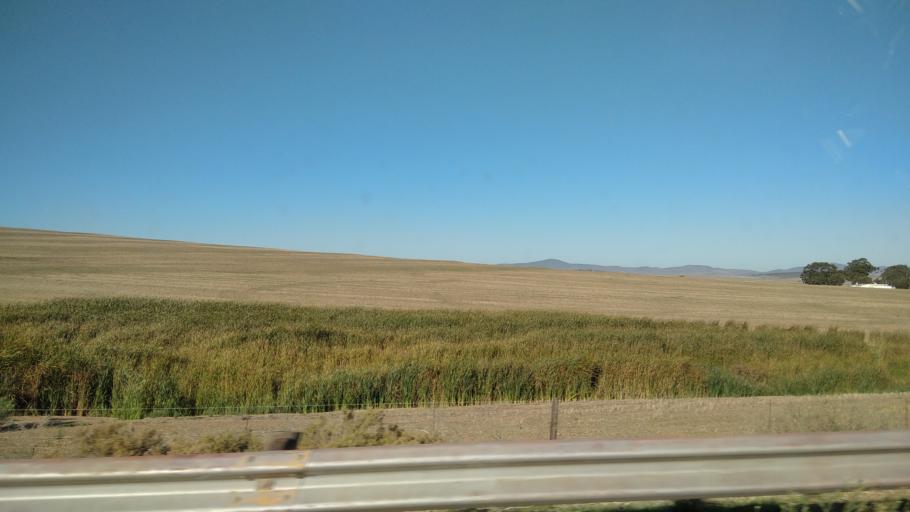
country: ZA
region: Western Cape
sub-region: West Coast District Municipality
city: Malmesbury
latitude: -33.3750
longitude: 18.6615
